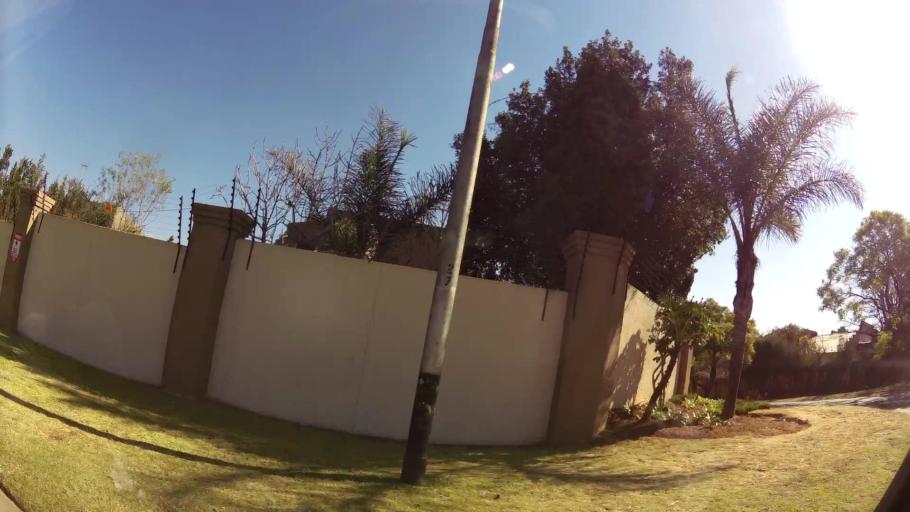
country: ZA
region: Gauteng
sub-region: City of Johannesburg Metropolitan Municipality
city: Johannesburg
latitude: -26.2692
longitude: 28.0266
